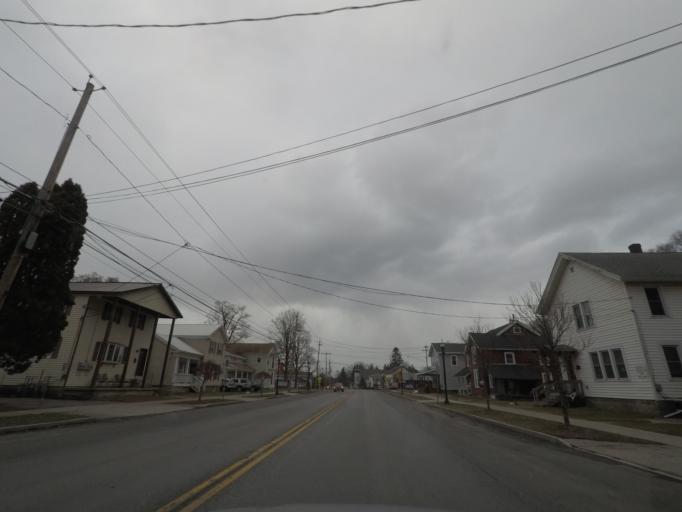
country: US
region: New York
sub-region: Madison County
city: Chittenango
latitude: 43.0481
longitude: -75.8660
